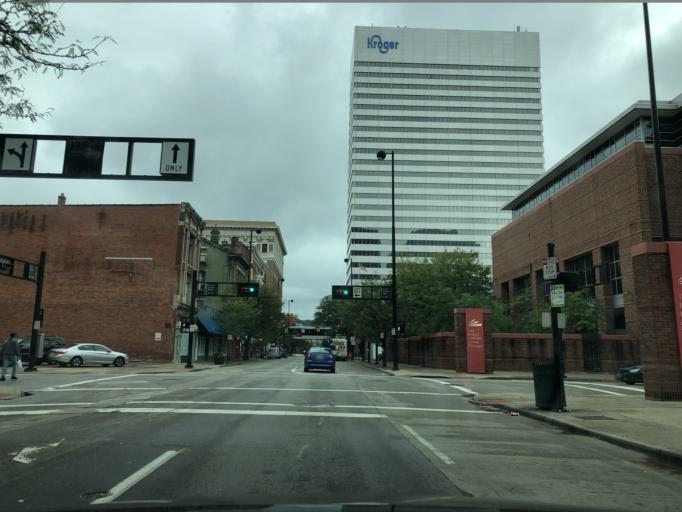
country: US
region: Kentucky
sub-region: Kenton County
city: Covington
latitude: 39.1051
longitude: -84.5139
